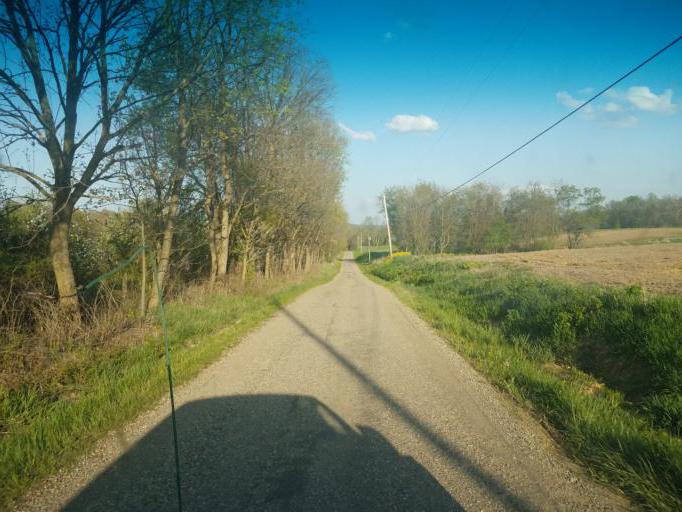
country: US
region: Ohio
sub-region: Holmes County
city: Millersburg
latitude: 40.5792
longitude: -81.9910
